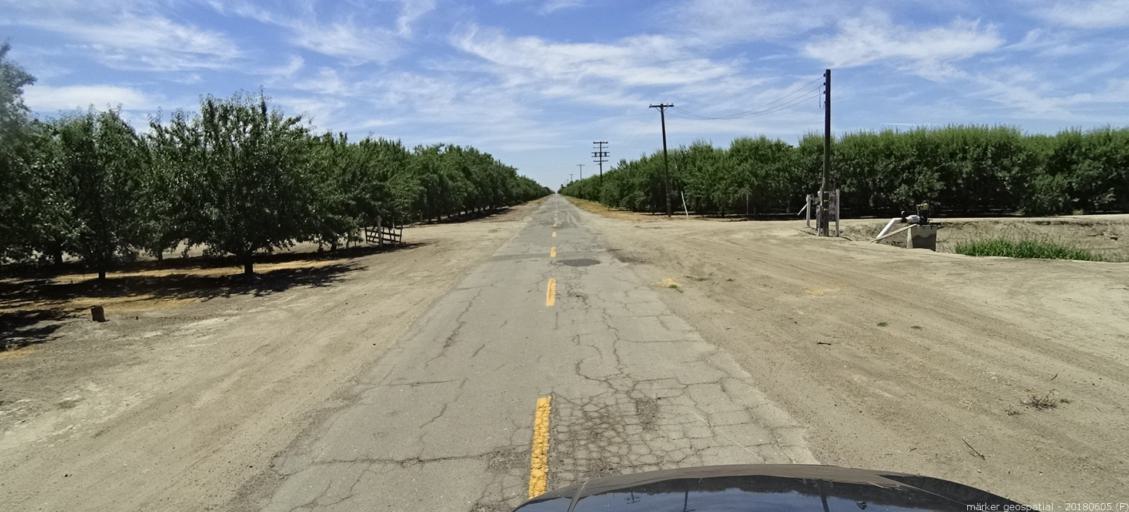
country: US
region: California
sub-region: Madera County
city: Chowchilla
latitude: 37.0906
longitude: -120.4117
